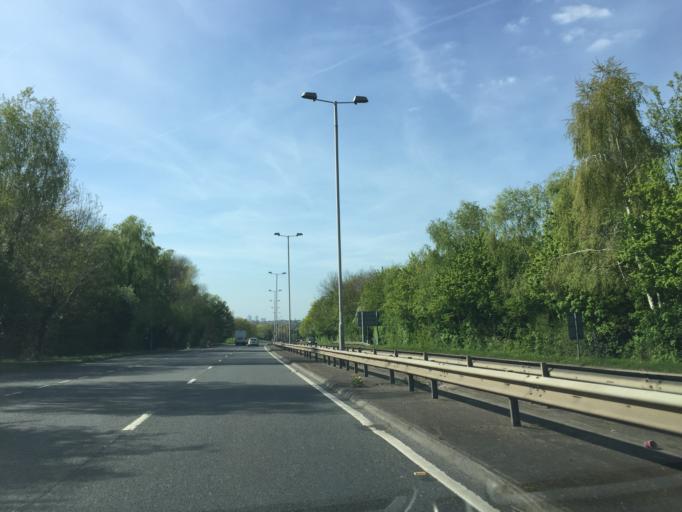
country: GB
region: England
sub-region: Greater London
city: Sidcup
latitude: 51.4233
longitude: 0.0904
